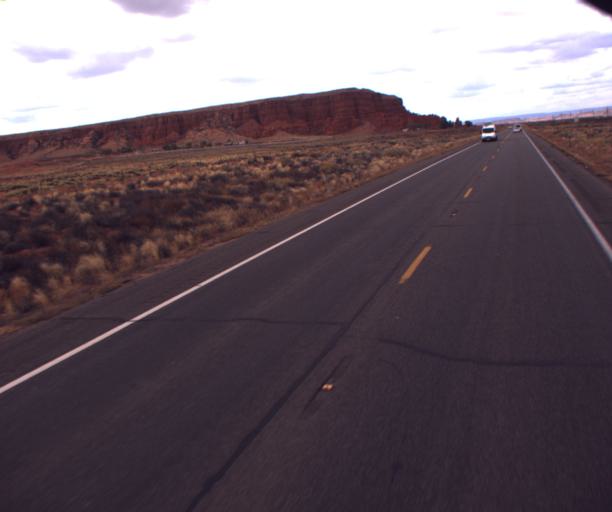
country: US
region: Arizona
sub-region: Navajo County
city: Kayenta
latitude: 36.7786
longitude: -110.0019
